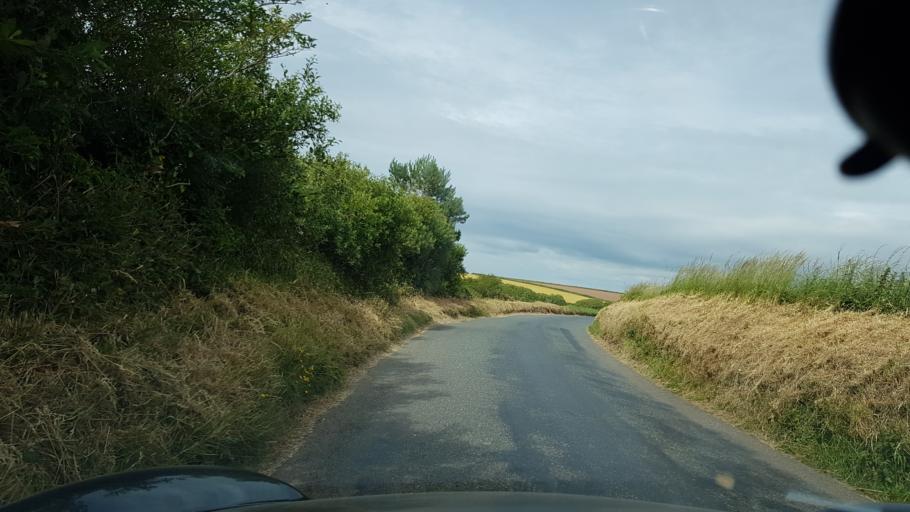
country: GB
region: Wales
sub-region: Pembrokeshire
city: Dale
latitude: 51.7298
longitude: -5.1892
